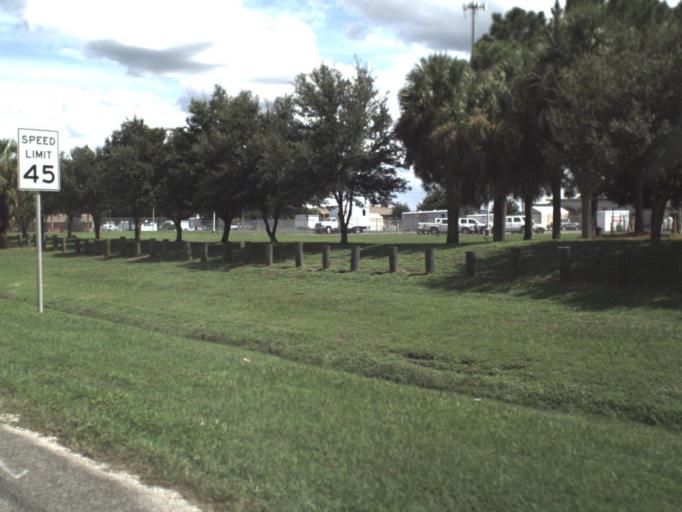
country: US
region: Florida
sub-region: Polk County
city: Bartow
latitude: 27.8967
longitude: -81.8621
